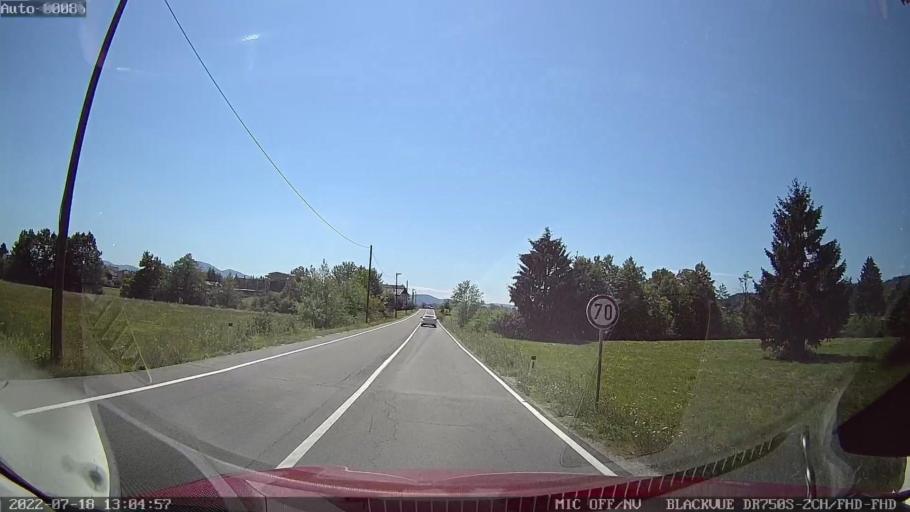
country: SI
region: Brezovica
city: Vnanje Gorice
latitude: 46.0412
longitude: 14.4443
